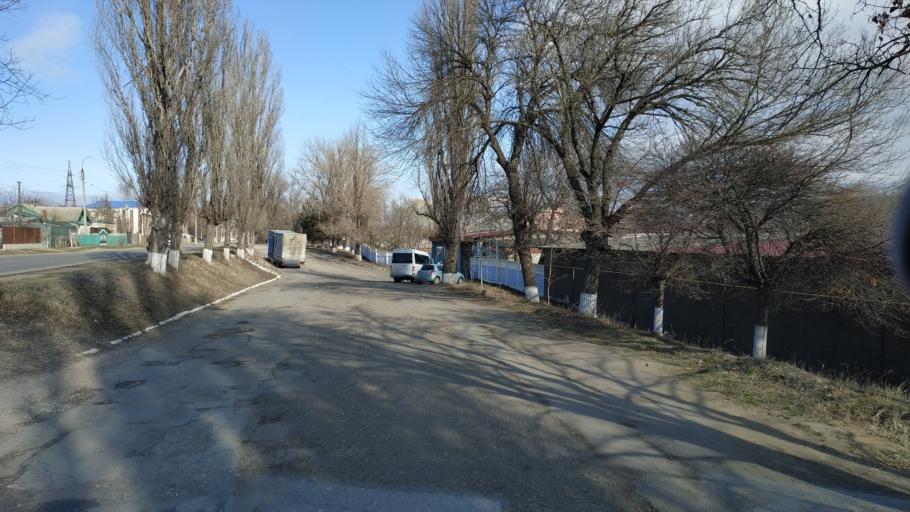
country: MD
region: Causeni
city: Causeni
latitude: 46.6587
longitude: 29.4205
